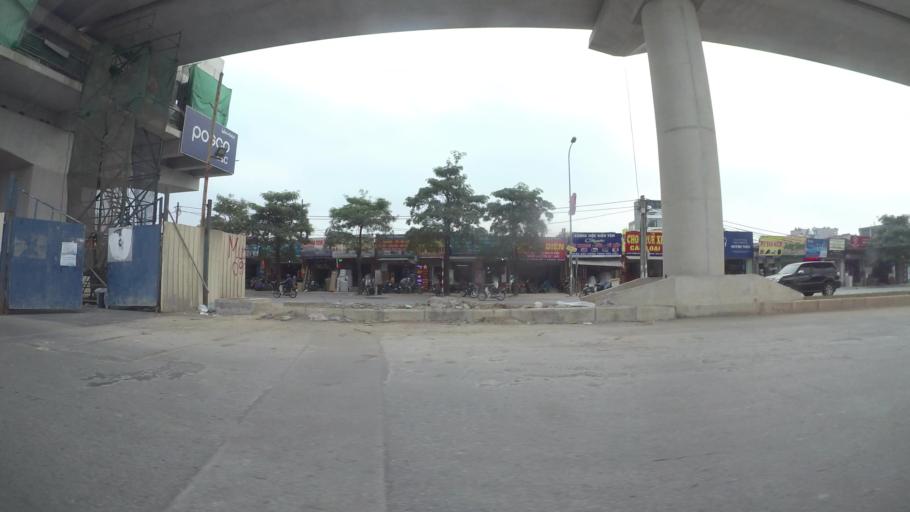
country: VN
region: Ha Noi
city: Cau Dien
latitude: 21.0443
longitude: 105.7546
